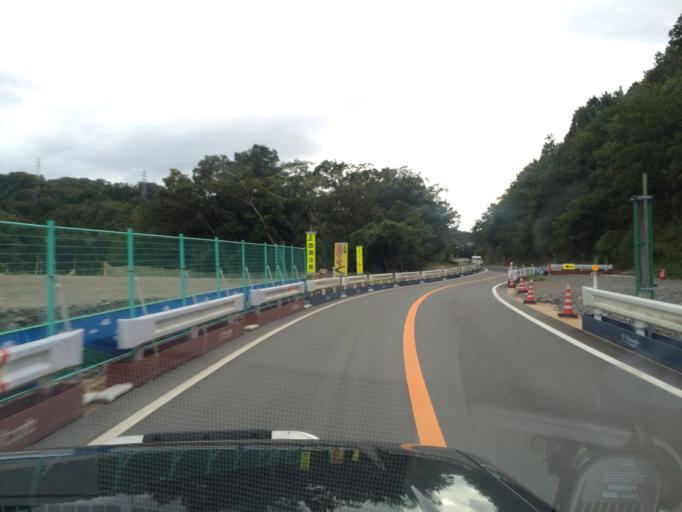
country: JP
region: Hyogo
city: Toyooka
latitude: 35.5081
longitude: 134.8025
